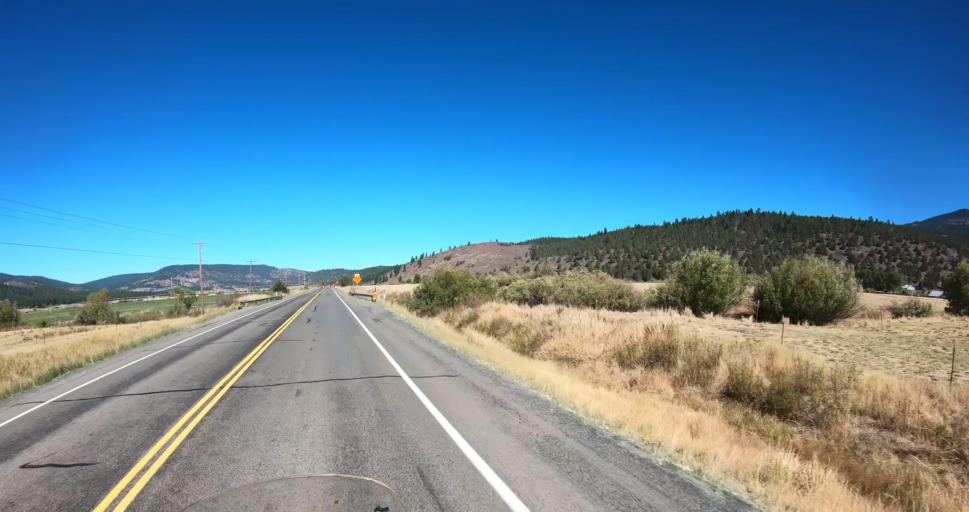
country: US
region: Oregon
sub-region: Lake County
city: Lakeview
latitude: 42.3394
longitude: -120.2976
